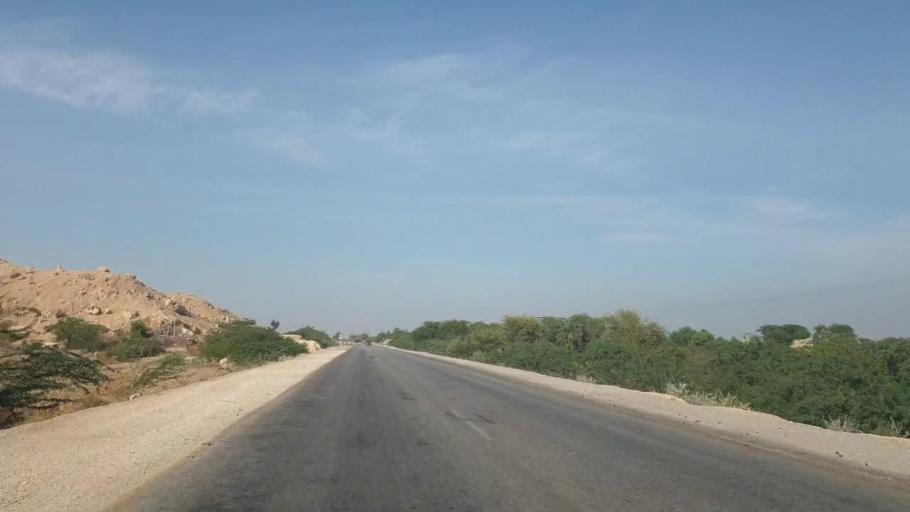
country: PK
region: Sindh
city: Sehwan
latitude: 26.3092
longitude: 67.8926
